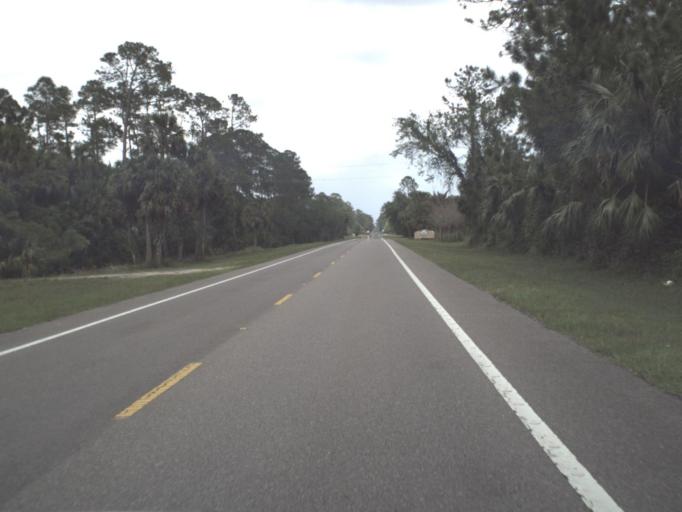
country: US
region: Florida
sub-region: Flagler County
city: Bunnell
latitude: 29.4516
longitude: -81.2709
